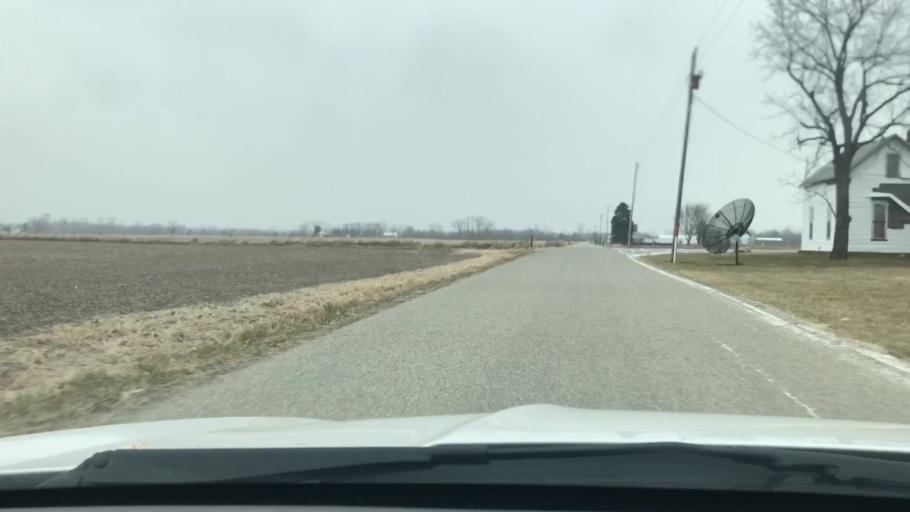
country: US
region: Indiana
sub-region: Fulton County
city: Akron
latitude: 41.0398
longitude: -86.0953
